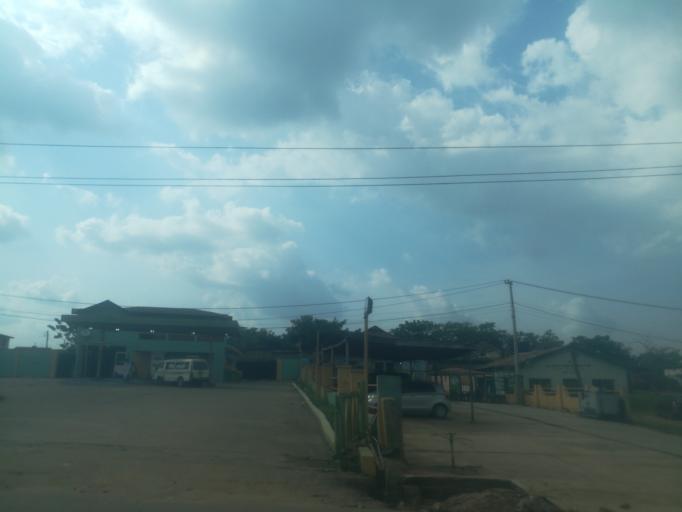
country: NG
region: Ogun
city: Abeokuta
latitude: 7.1387
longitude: 3.3118
